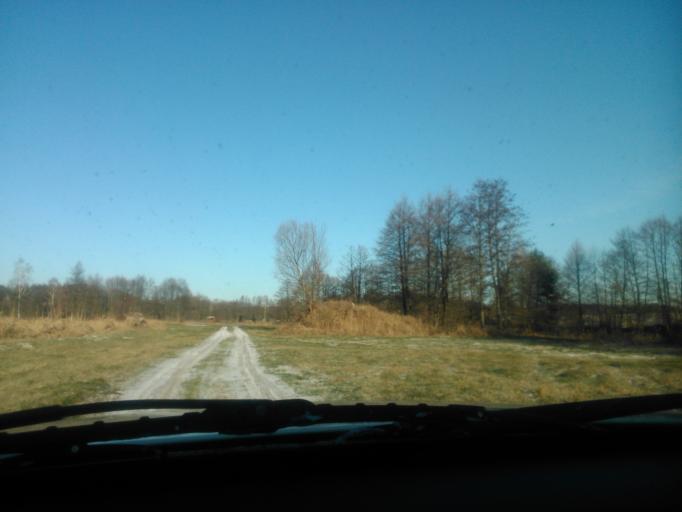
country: PL
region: Warmian-Masurian Voivodeship
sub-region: Powiat nowomiejski
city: Kurzetnik
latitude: 53.3663
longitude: 19.5251
